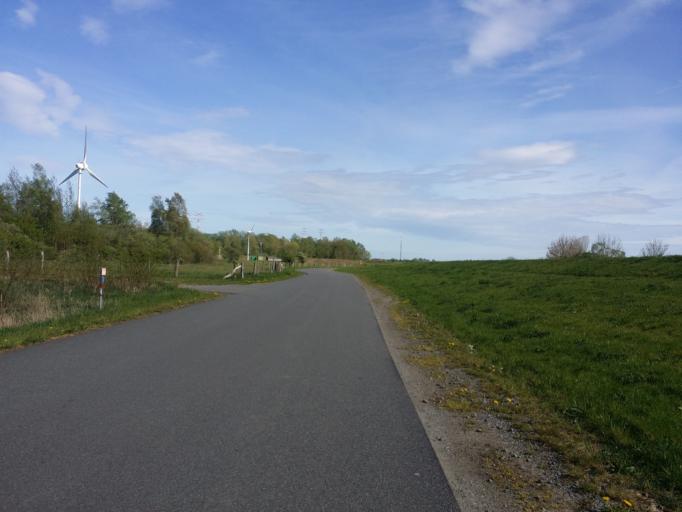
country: DE
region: Lower Saxony
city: Lemwerder
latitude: 53.1323
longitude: 8.6433
